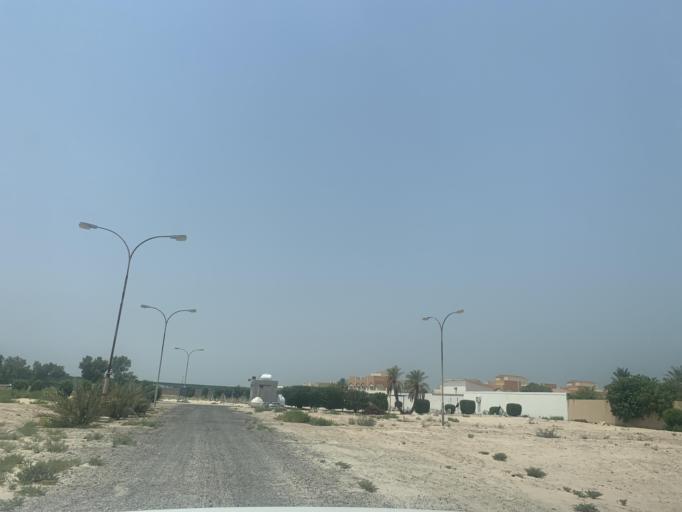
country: BH
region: Central Governorate
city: Madinat Hamad
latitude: 26.1471
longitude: 50.4585
